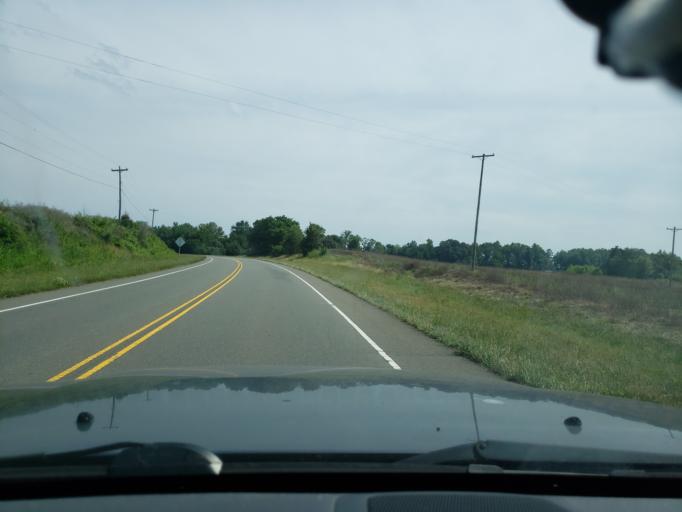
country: US
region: North Carolina
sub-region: Alamance County
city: Saxapahaw
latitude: 35.9746
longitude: -79.2799
